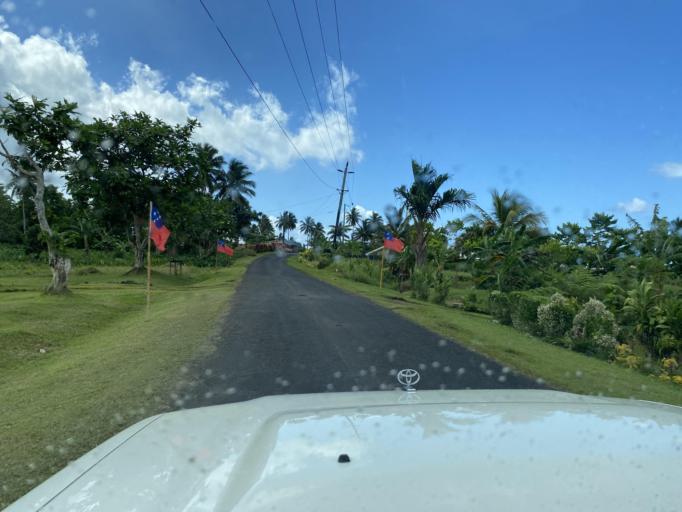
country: WS
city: Matavai
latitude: -13.9889
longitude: -171.5868
